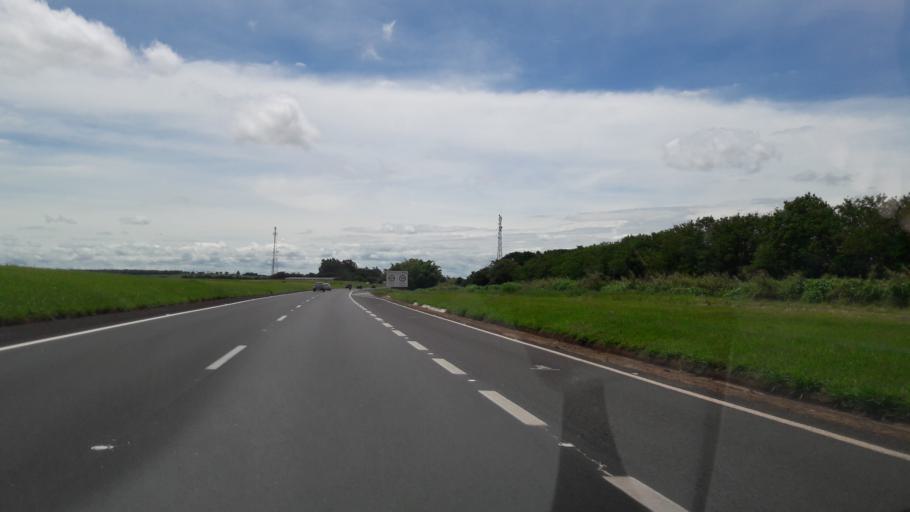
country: BR
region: Sao Paulo
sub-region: Avare
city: Avare
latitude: -22.9574
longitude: -48.8542
